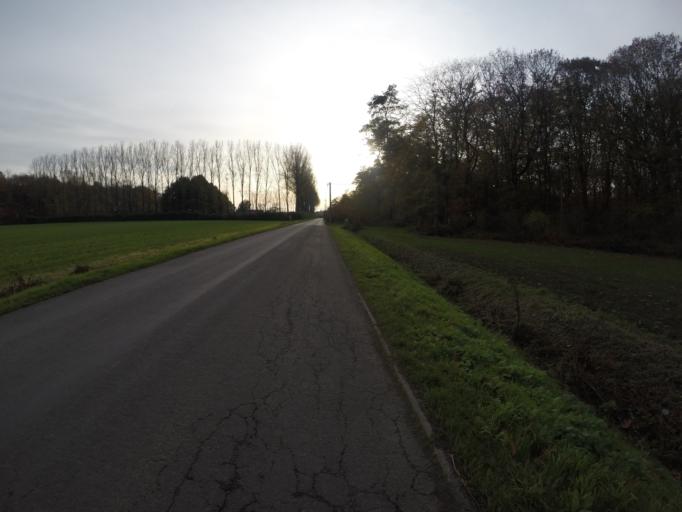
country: BE
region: Flanders
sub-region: Provincie Oost-Vlaanderen
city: Aalter
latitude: 51.0658
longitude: 3.4751
